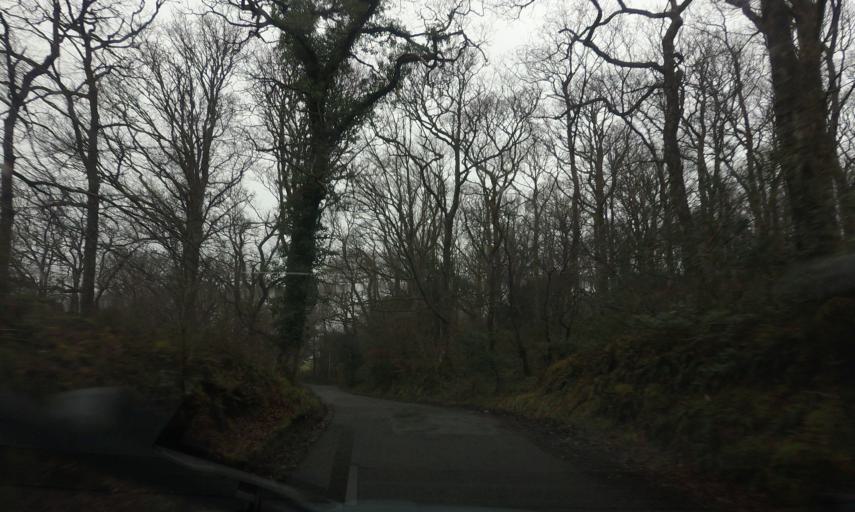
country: GB
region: Scotland
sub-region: West Dunbartonshire
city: Balloch
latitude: 56.1353
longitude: -4.6128
